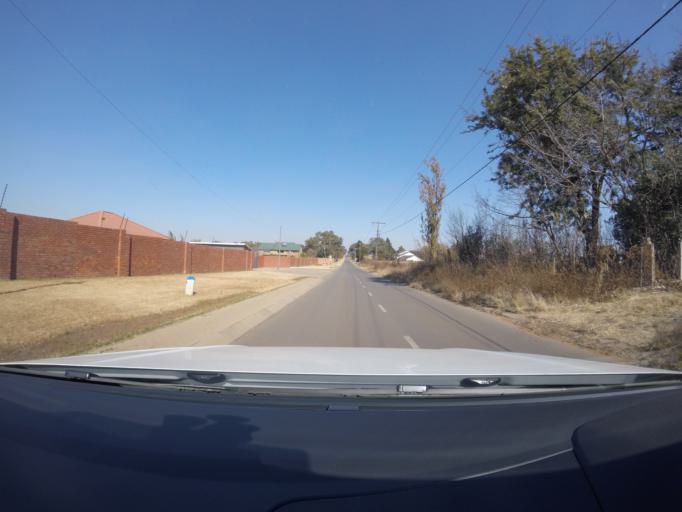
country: ZA
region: Gauteng
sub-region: Ekurhuleni Metropolitan Municipality
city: Benoni
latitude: -26.1214
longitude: 28.3005
